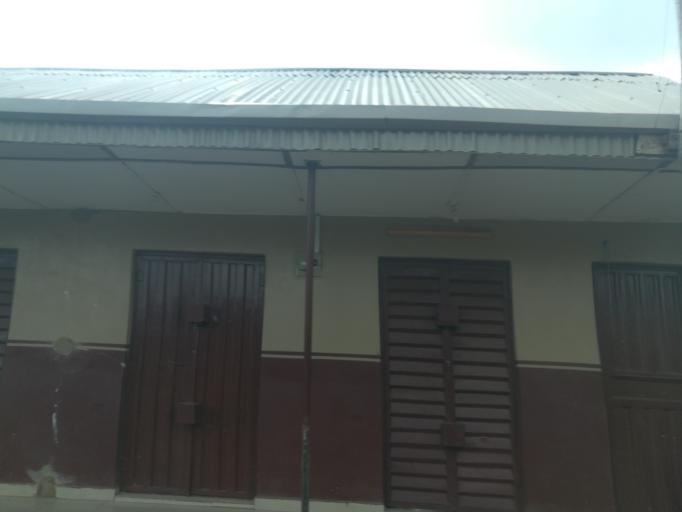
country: NG
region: Oyo
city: Ibadan
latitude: 7.3322
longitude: 3.8585
